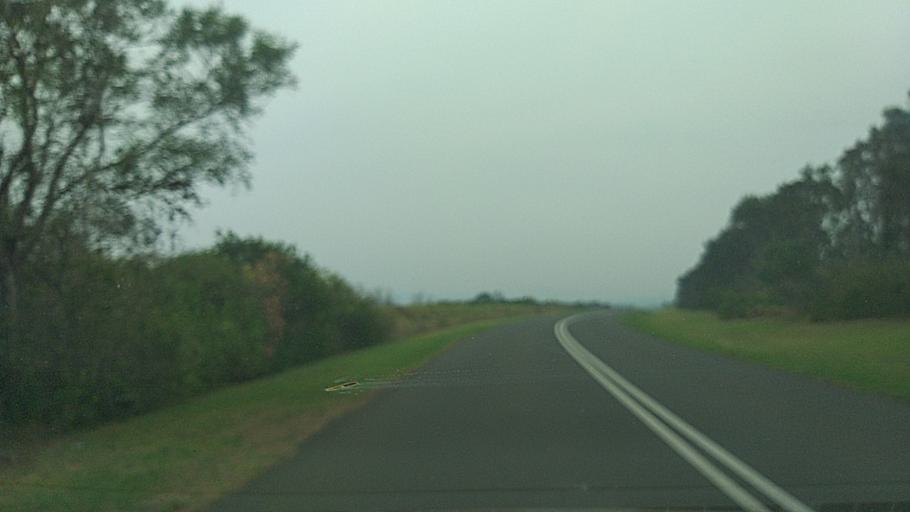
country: AU
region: New South Wales
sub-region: Shellharbour
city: Croom
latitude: -34.6070
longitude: 150.8615
